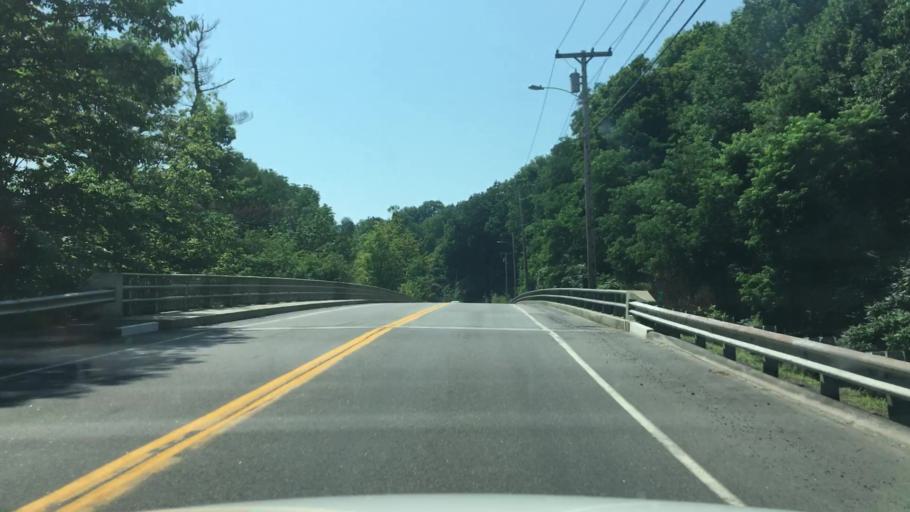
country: US
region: Maine
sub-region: Kennebec County
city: Hallowell
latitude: 44.2743
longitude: -69.7918
